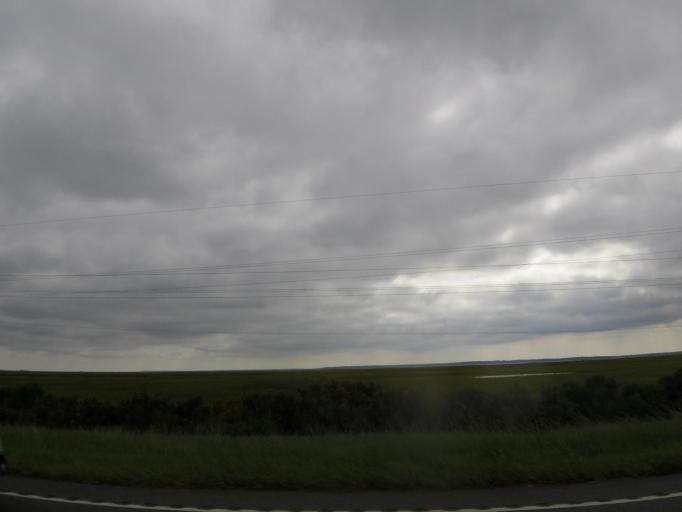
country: US
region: Georgia
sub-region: Glynn County
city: Brunswick
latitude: 31.0726
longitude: -81.4644
